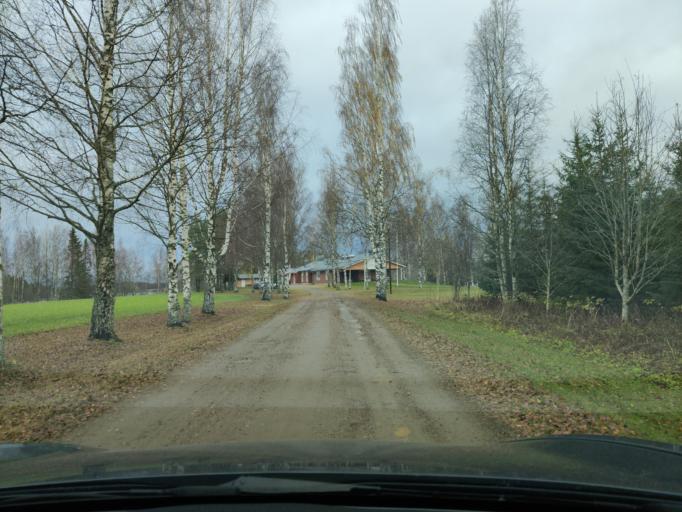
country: FI
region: Northern Savo
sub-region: Ylae-Savo
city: Kiuruvesi
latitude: 63.6408
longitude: 26.6547
